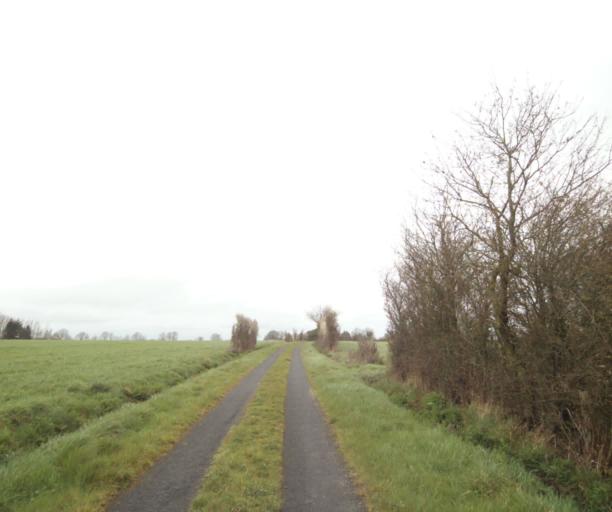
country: FR
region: Pays de la Loire
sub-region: Departement de la Loire-Atlantique
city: Bouvron
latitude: 47.4393
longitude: -1.8776
